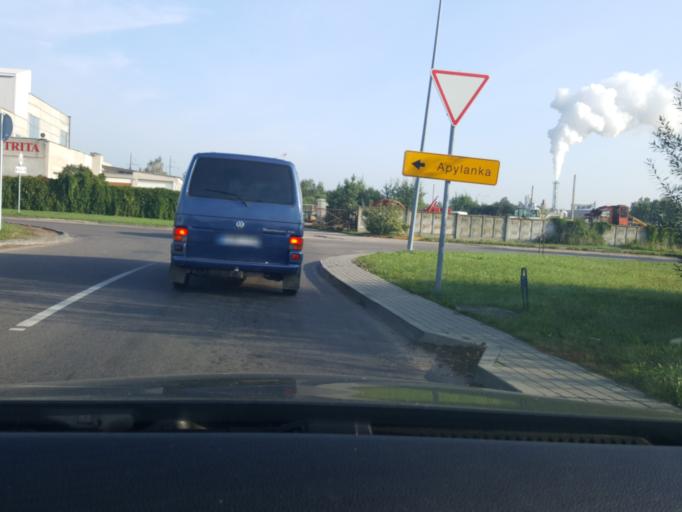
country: LT
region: Alytaus apskritis
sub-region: Alytus
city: Alytus
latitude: 54.4370
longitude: 24.0179
